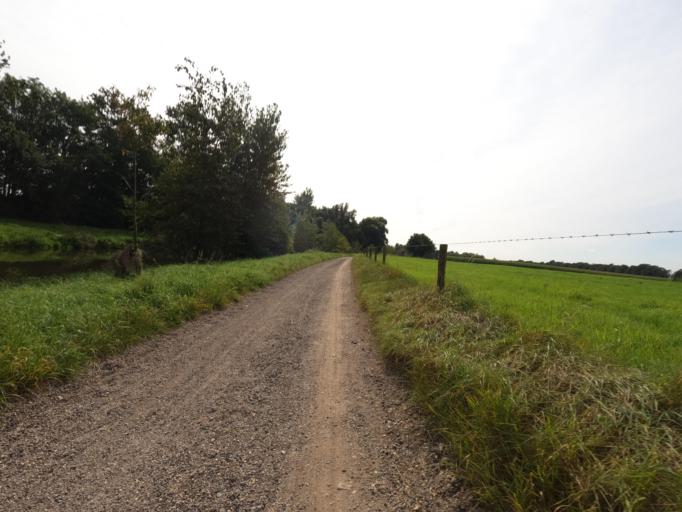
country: DE
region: North Rhine-Westphalia
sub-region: Regierungsbezirk Koln
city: Linnich
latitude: 51.0196
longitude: 6.2547
